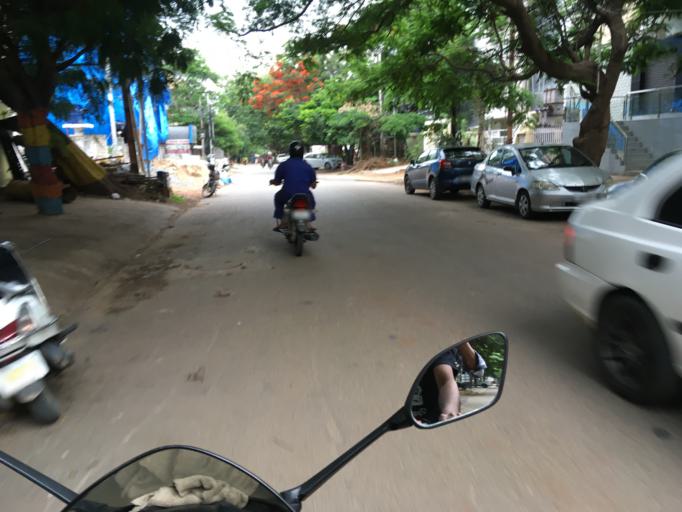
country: IN
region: Telangana
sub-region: Rangareddi
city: Kukatpalli
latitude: 17.4501
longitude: 78.3857
